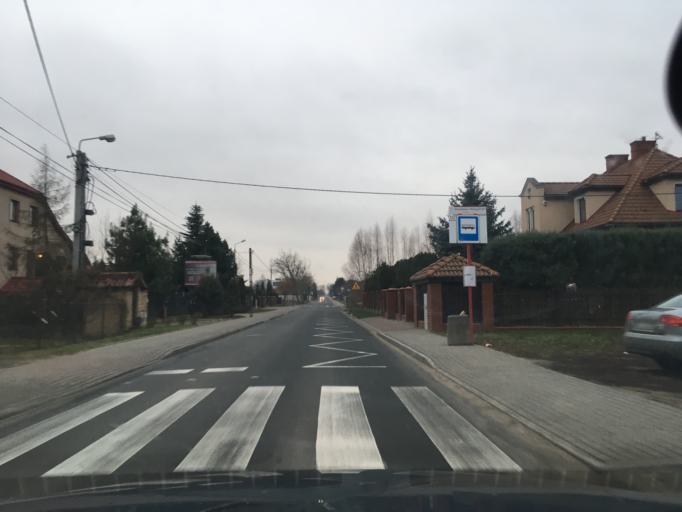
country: PL
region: Masovian Voivodeship
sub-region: Powiat piaseczynski
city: Mysiadlo
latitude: 52.1300
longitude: 20.9798
